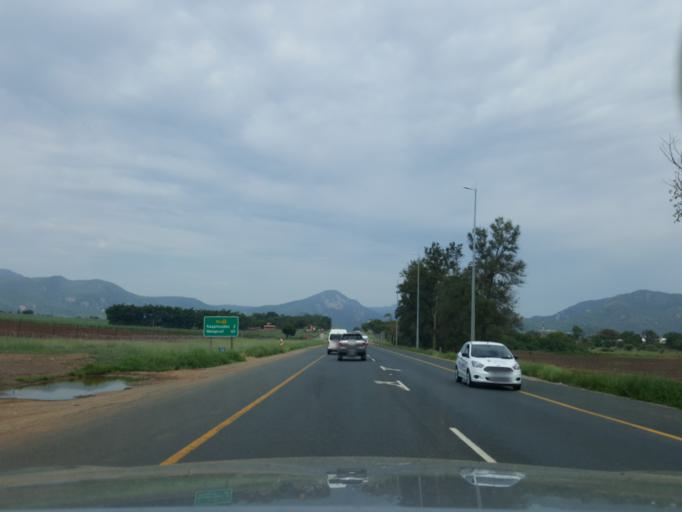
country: SZ
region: Hhohho
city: Ntfonjeni
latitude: -25.5365
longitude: 31.3397
